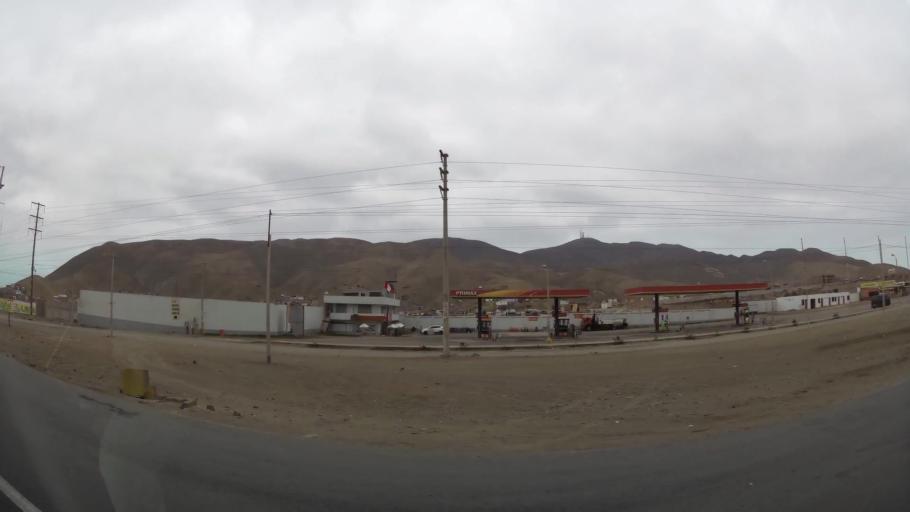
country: PE
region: Lima
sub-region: Lima
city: Pucusana
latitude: -12.4603
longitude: -76.7528
